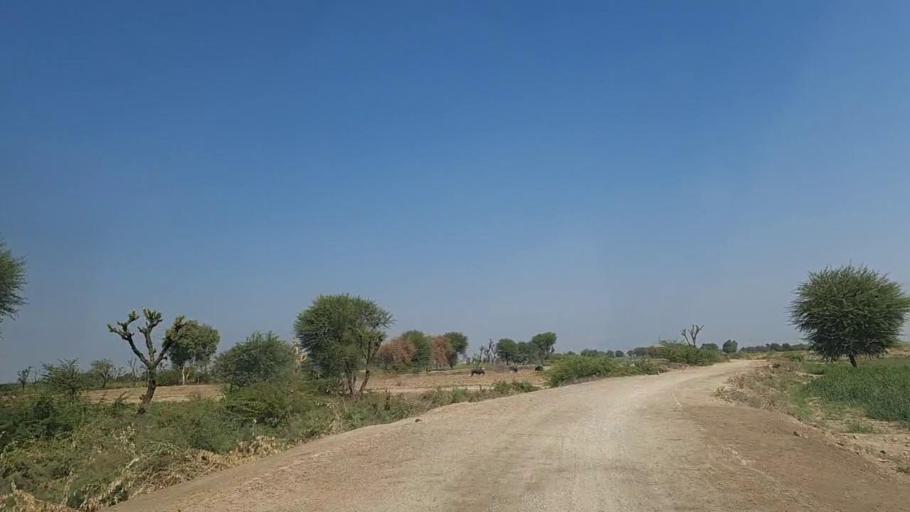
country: PK
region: Sindh
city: Digri
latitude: 25.2005
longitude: 69.1398
